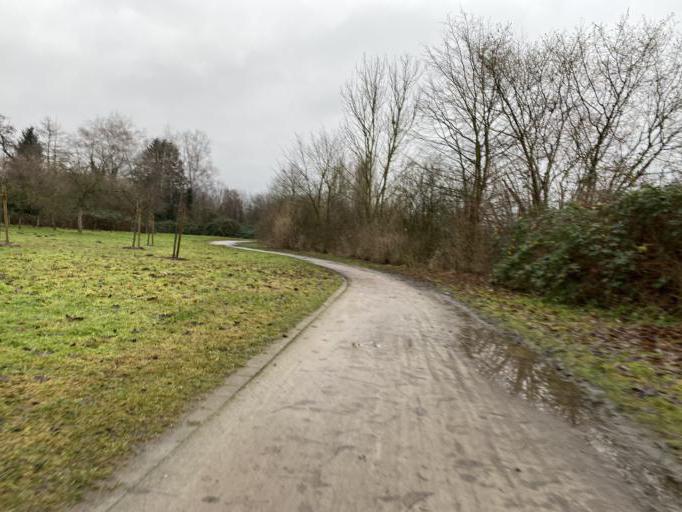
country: DE
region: North Rhine-Westphalia
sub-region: Regierungsbezirk Arnsberg
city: Hamm
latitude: 51.6846
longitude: 7.8005
